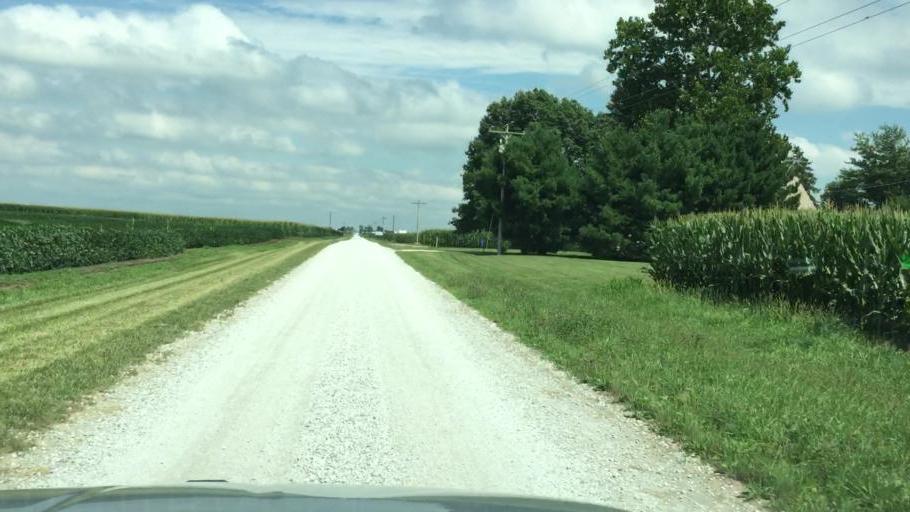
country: US
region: Illinois
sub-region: Hancock County
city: Nauvoo
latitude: 40.5216
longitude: -91.2926
